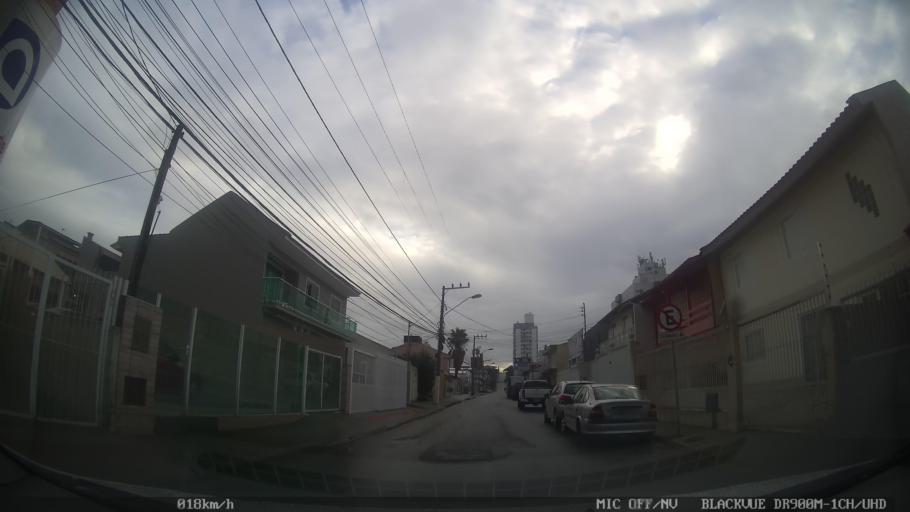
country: BR
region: Santa Catarina
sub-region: Sao Jose
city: Campinas
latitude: -27.5870
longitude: -48.6108
